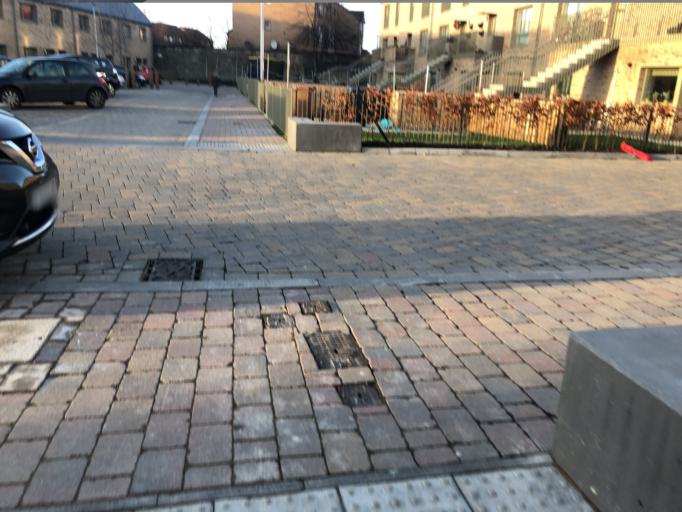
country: GB
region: Scotland
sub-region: Edinburgh
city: Edinburgh
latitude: 55.9772
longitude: -3.1843
